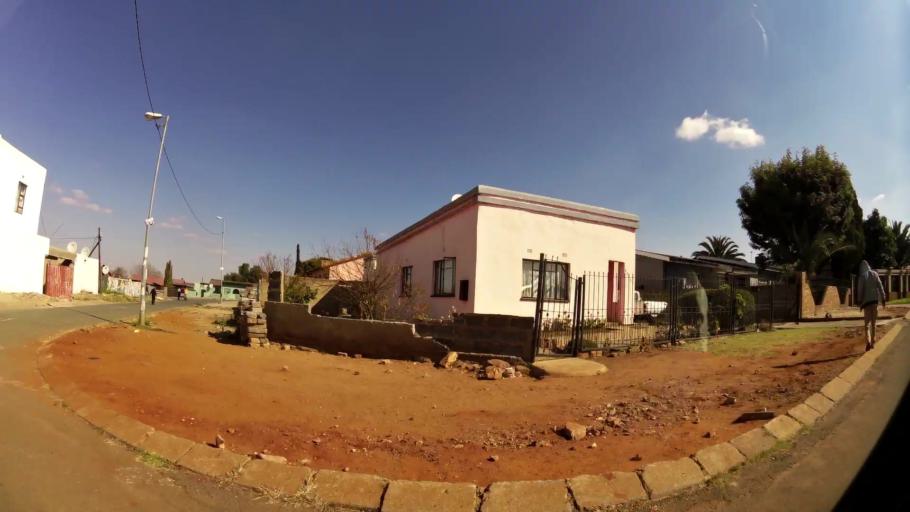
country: ZA
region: Gauteng
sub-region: City of Johannesburg Metropolitan Municipality
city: Soweto
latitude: -26.2387
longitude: 27.9040
